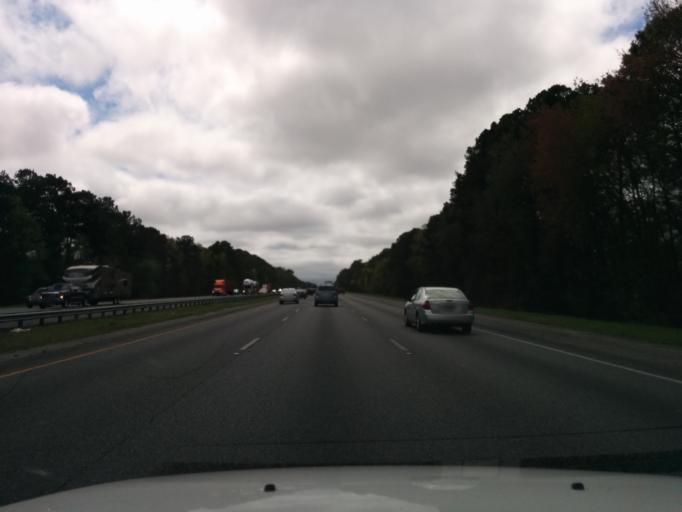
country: US
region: Georgia
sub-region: Chatham County
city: Pooler
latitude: 32.0515
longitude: -81.2576
